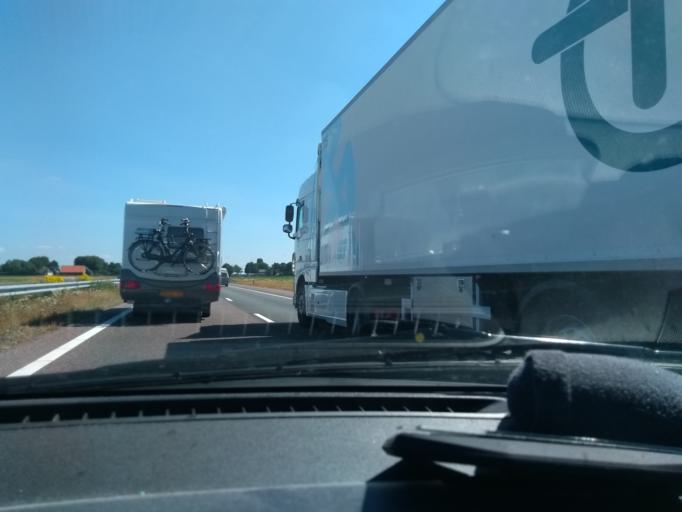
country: NL
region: Drenthe
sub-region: Gemeente Emmen
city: Emmen
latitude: 52.7232
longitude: 6.9177
